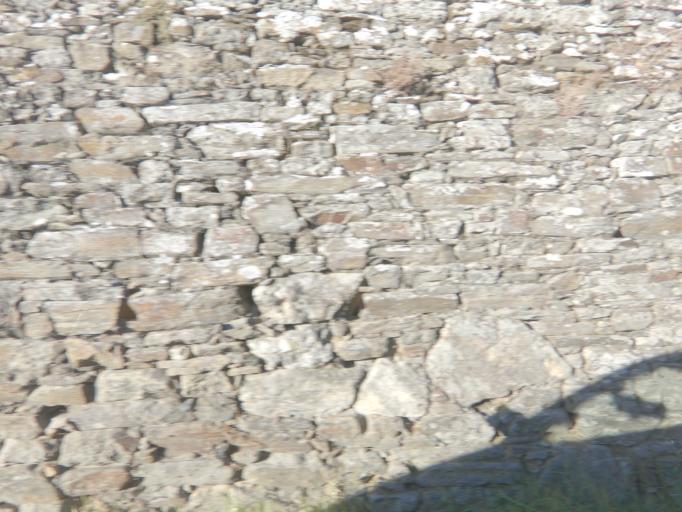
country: PT
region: Vila Real
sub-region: Peso da Regua
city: Godim
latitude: 41.1619
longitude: -7.8242
